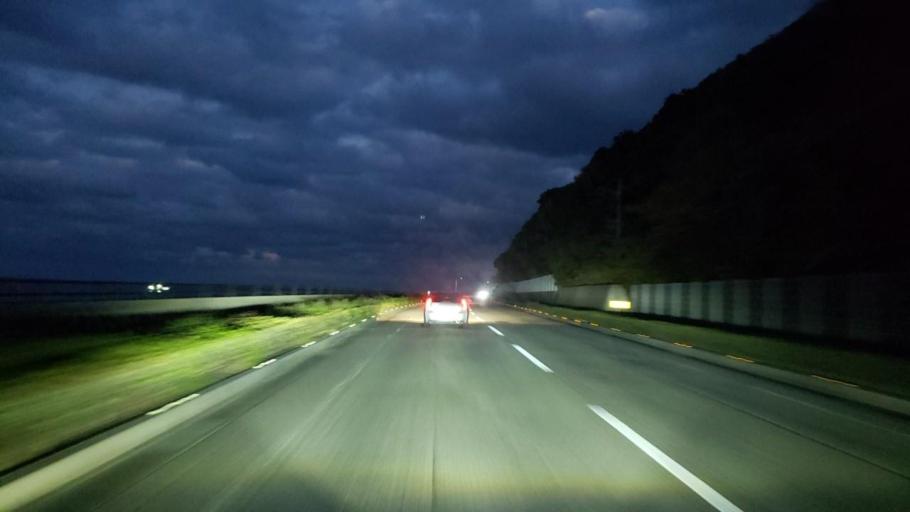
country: JP
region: Tokushima
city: Narutocho-mitsuishi
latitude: 34.2215
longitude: 134.4911
